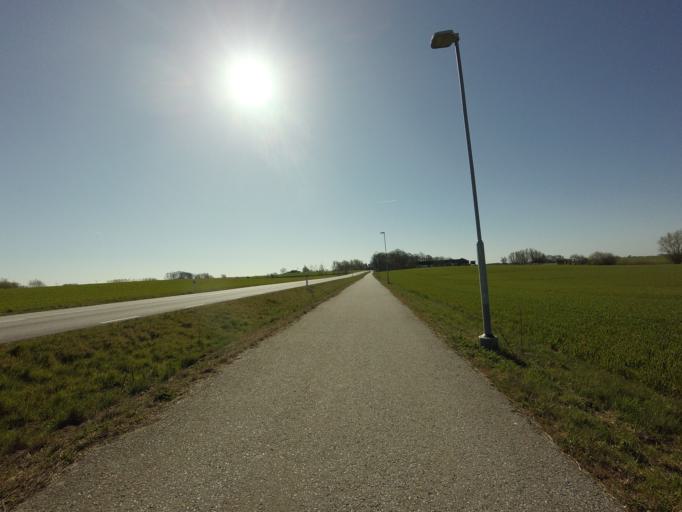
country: SE
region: Skane
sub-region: Malmo
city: Oxie
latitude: 55.4868
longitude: 13.1228
